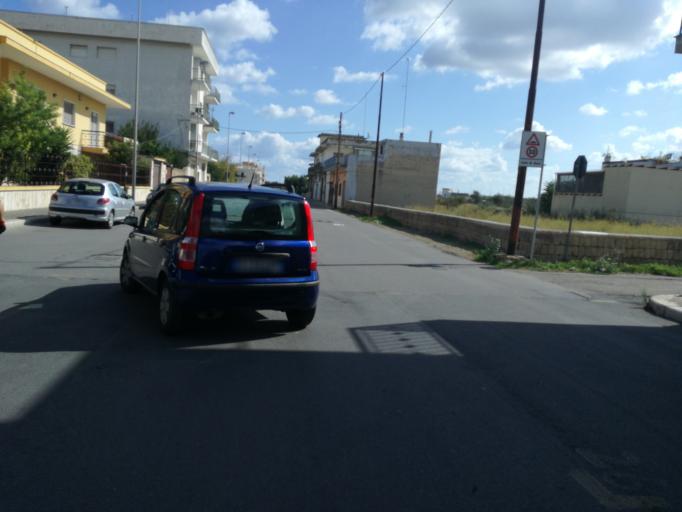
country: IT
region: Apulia
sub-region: Provincia di Bari
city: Triggiano
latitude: 41.0639
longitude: 16.9306
